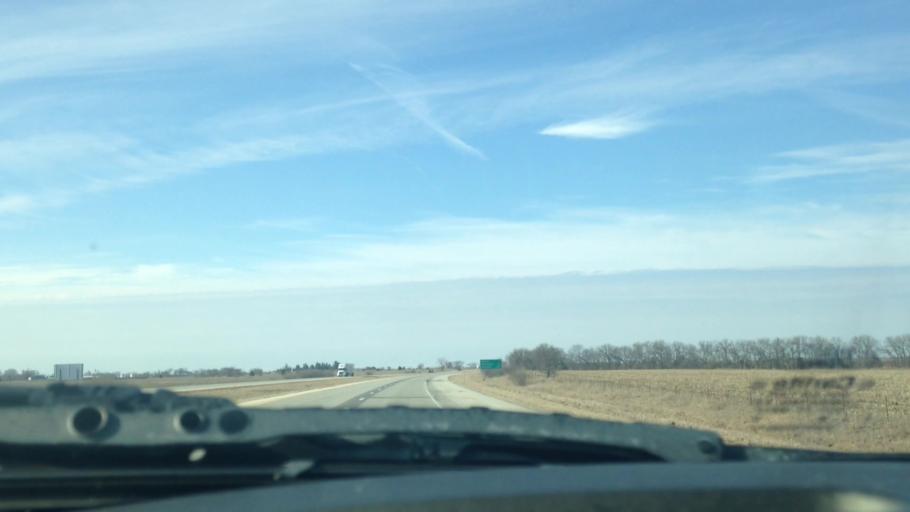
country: US
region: Illinois
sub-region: Ford County
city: Paxton
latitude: 40.5439
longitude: -88.0656
